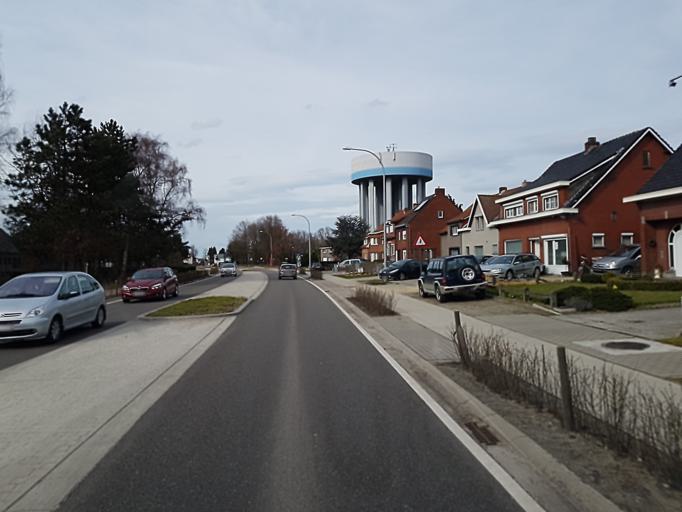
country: BE
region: Flanders
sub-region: Provincie Antwerpen
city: Dessel
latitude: 51.2505
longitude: 5.1076
